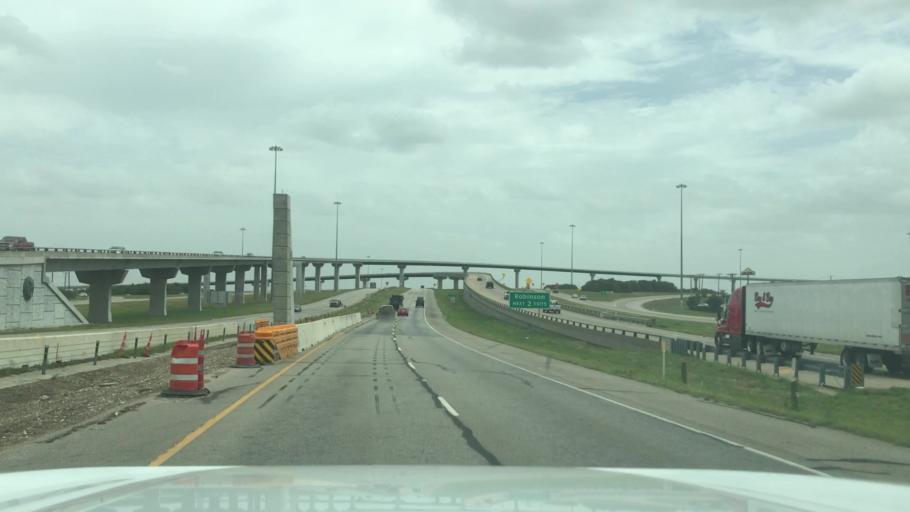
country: US
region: Texas
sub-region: McLennan County
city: Beverly Hills
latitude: 31.4958
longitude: -97.1574
